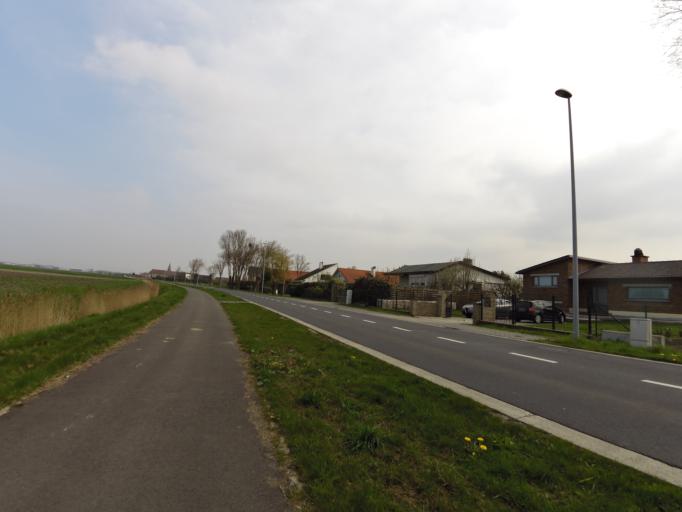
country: BE
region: Flanders
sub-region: Provincie West-Vlaanderen
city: Middelkerke
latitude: 51.1773
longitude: 2.8329
